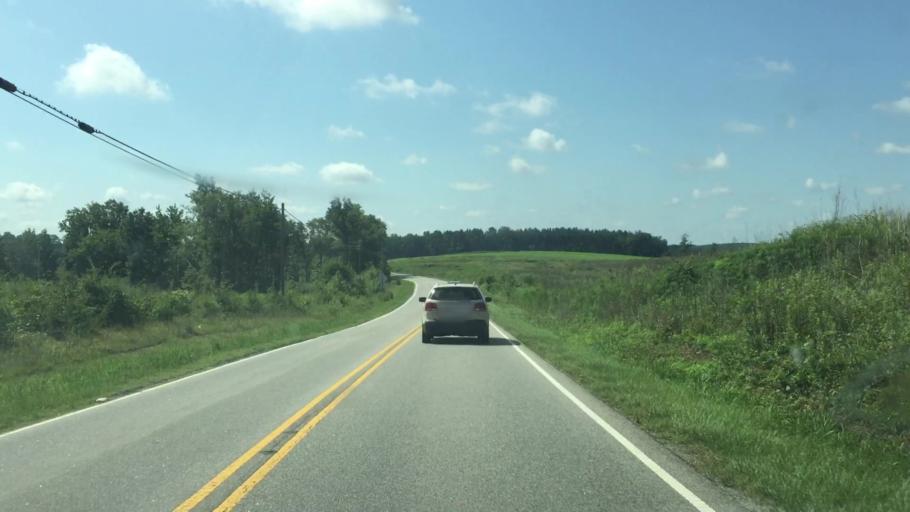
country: US
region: North Carolina
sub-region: Anson County
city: Polkton
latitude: 35.0160
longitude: -80.2193
